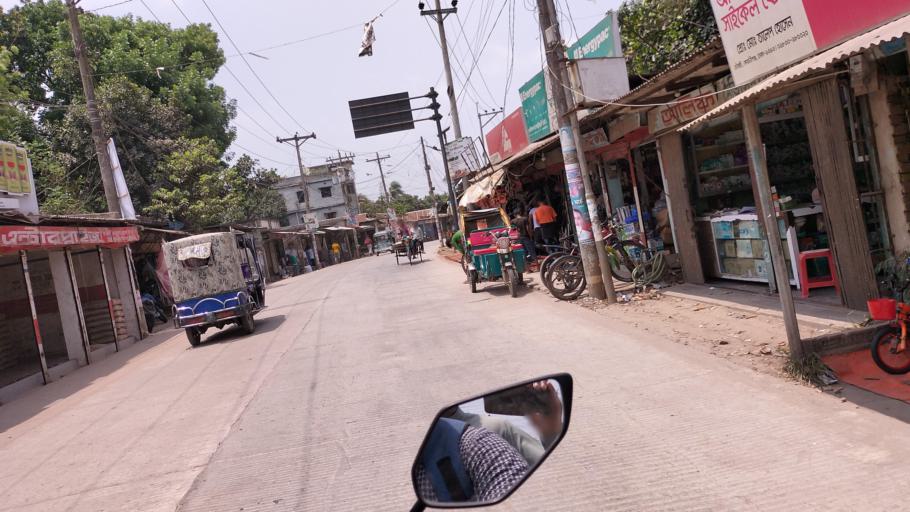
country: BD
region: Dhaka
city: Azimpur
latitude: 23.7329
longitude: 90.2728
